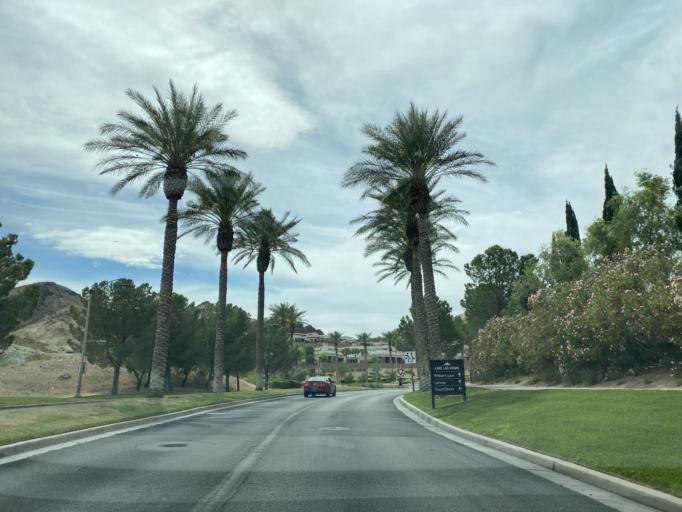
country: US
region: Nevada
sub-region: Clark County
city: Henderson
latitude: 36.0994
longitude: -114.9330
